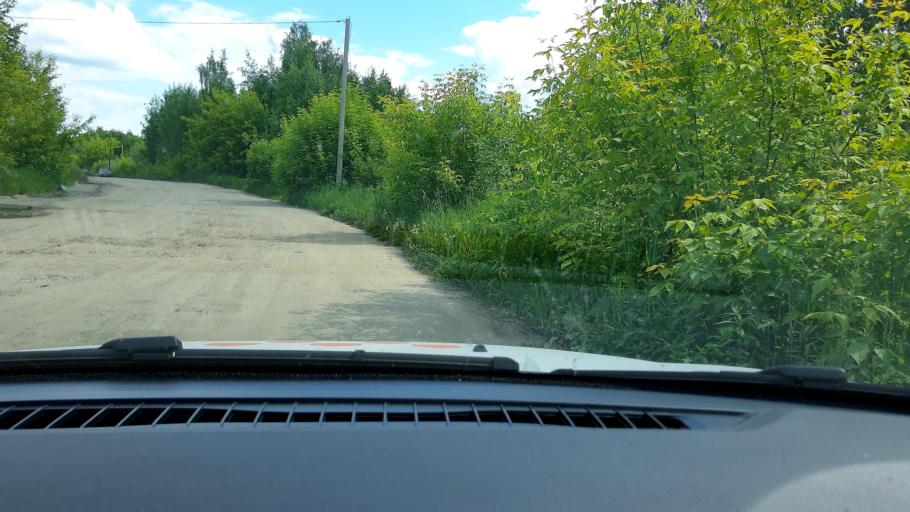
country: RU
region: Nizjnij Novgorod
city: Kstovo
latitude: 56.1703
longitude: 44.1621
